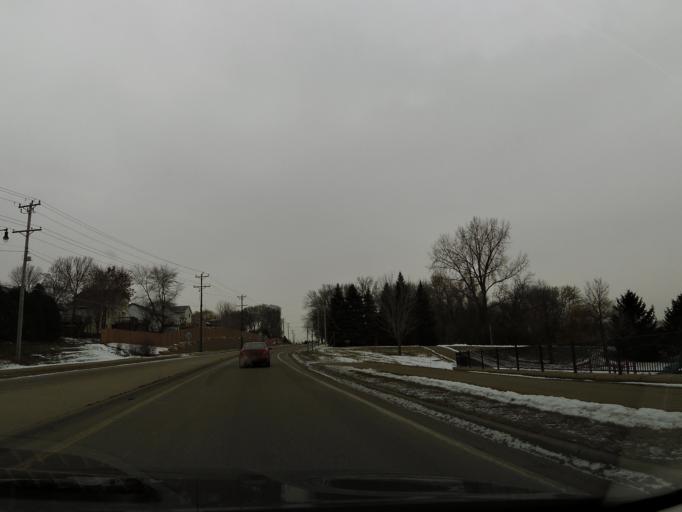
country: US
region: Minnesota
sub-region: Carver County
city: Waconia
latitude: 44.8361
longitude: -93.7887
